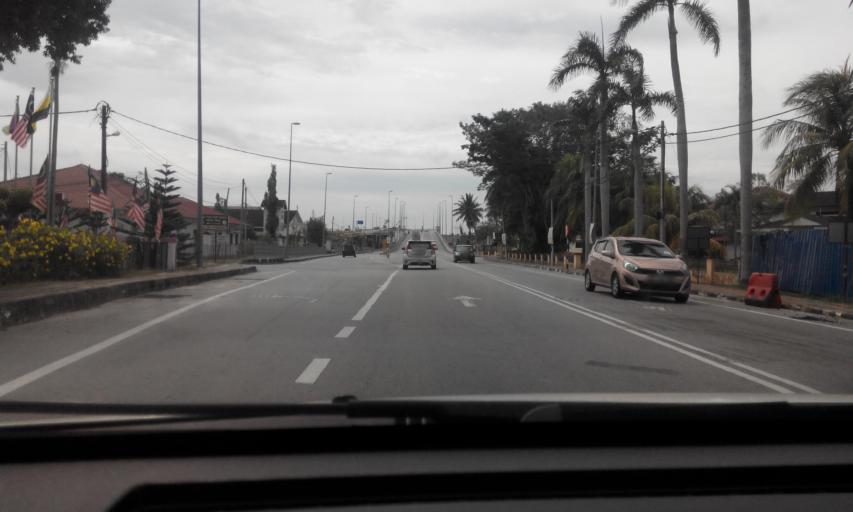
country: MY
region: Perak
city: Parit Buntar
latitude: 5.1302
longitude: 100.4898
